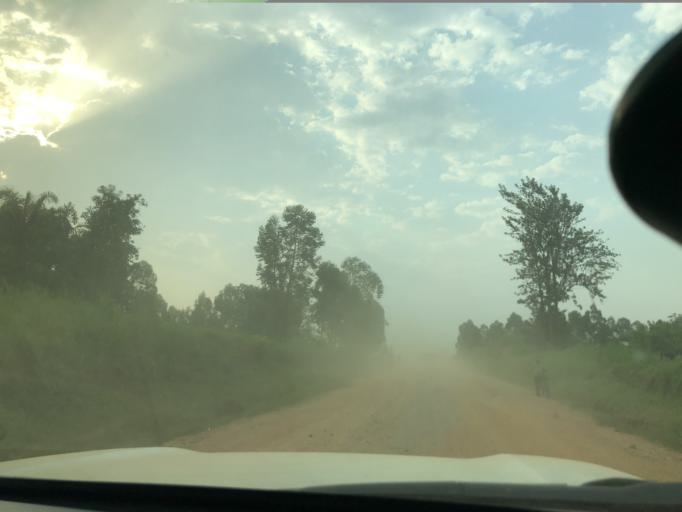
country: UG
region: Western Region
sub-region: Kasese District
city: Margherita
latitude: 0.3404
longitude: 29.6698
